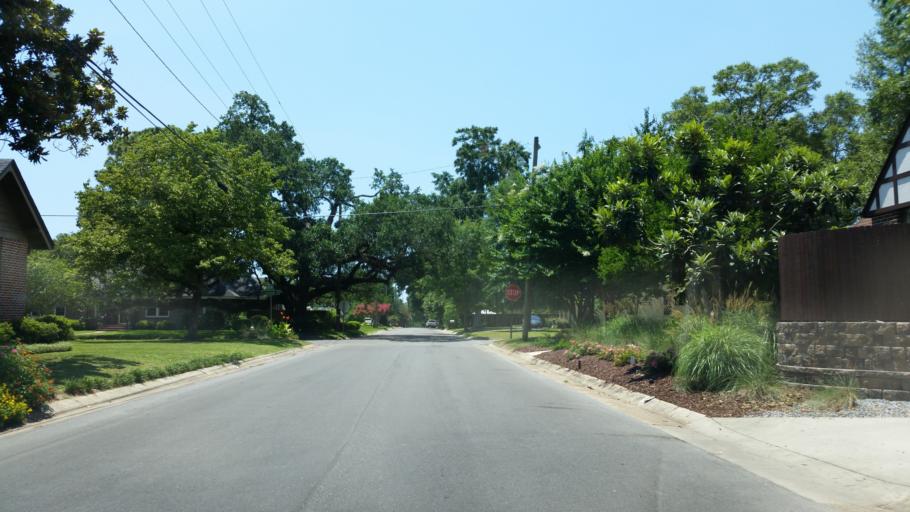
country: US
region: Florida
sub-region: Escambia County
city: East Pensacola Heights
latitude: 30.4369
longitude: -87.1918
